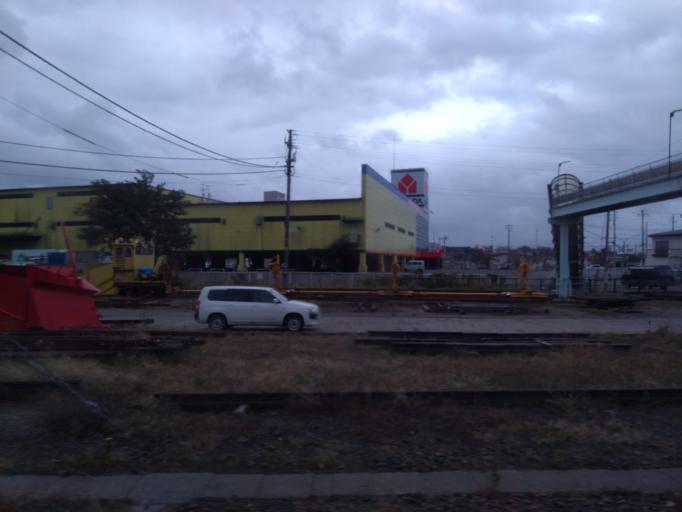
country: JP
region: Hokkaido
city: Hakodate
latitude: 41.8053
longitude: 140.7332
